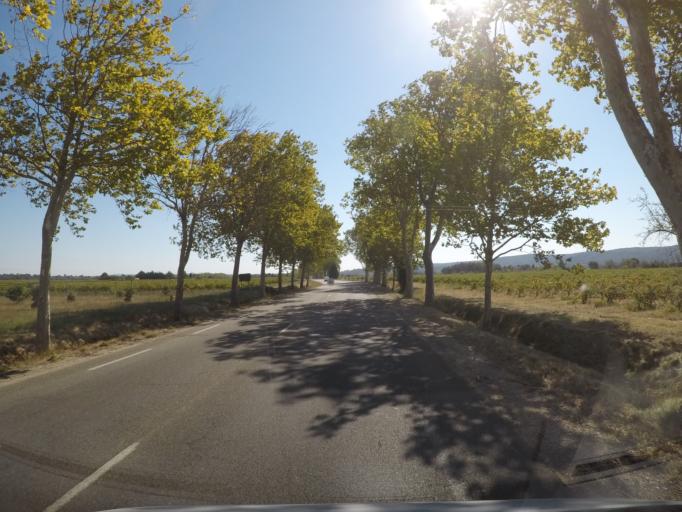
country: FR
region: Languedoc-Roussillon
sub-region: Departement du Gard
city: Castillon-du-Gard
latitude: 43.9700
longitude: 4.5012
